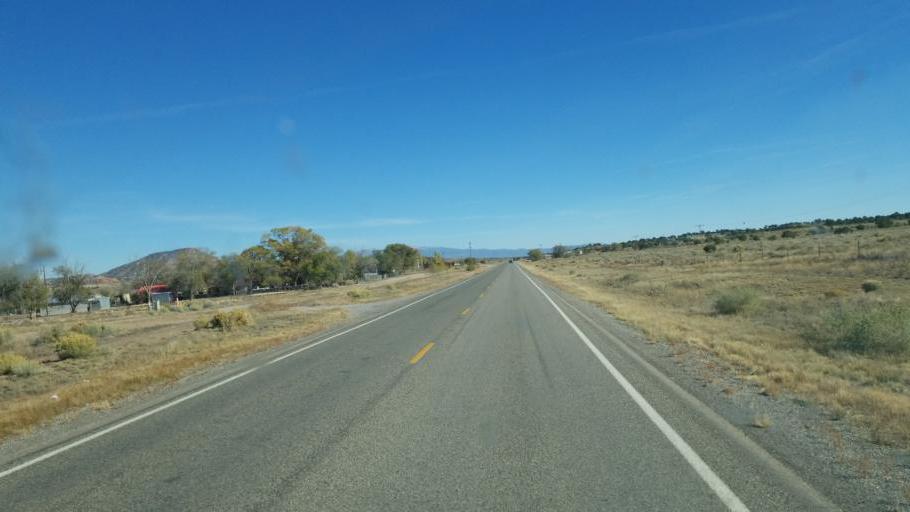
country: US
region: New Mexico
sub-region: McKinley County
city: Thoreau
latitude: 35.3596
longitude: -108.0315
